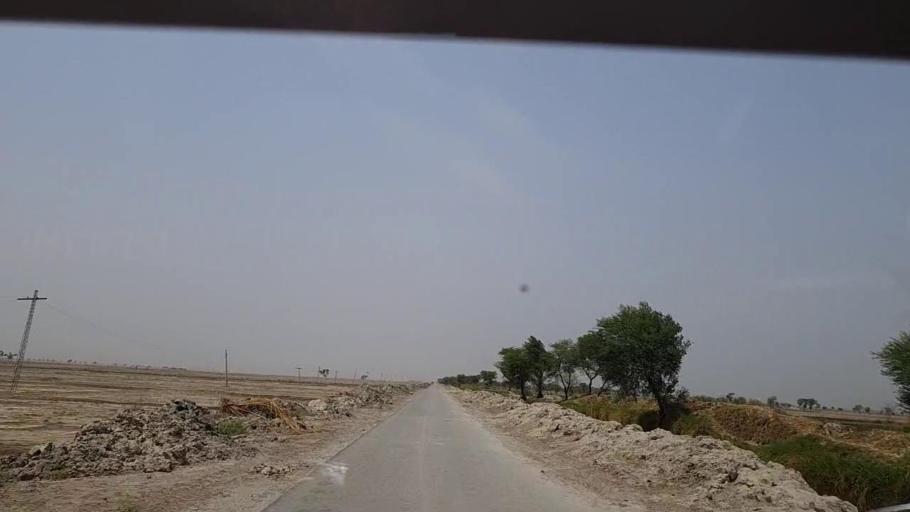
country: PK
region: Sindh
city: Khairpur Nathan Shah
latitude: 27.0210
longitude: 67.6215
